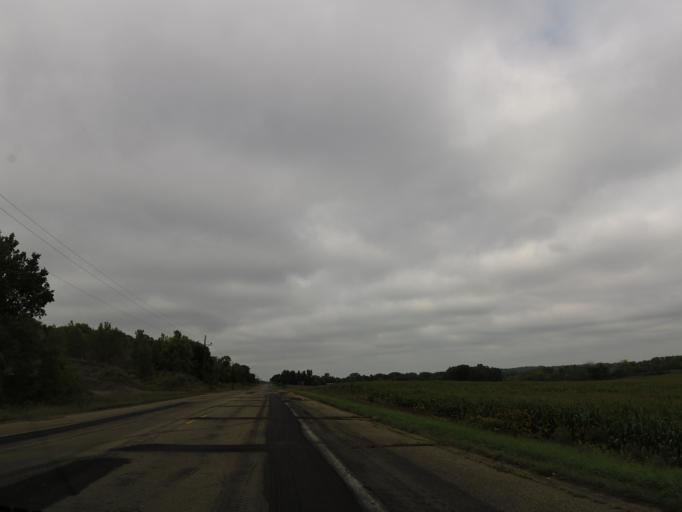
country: US
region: Minnesota
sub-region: Yellow Medicine County
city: Granite Falls
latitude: 44.8399
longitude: -95.6132
